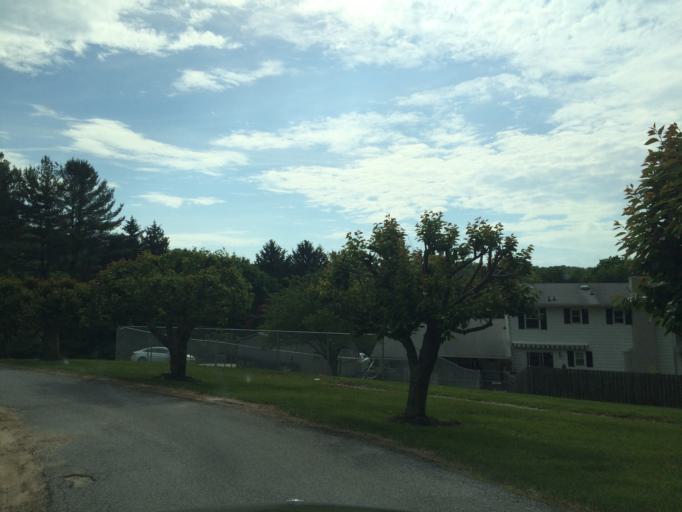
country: US
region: Maryland
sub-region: Baltimore County
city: Reisterstown
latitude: 39.4048
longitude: -76.8580
